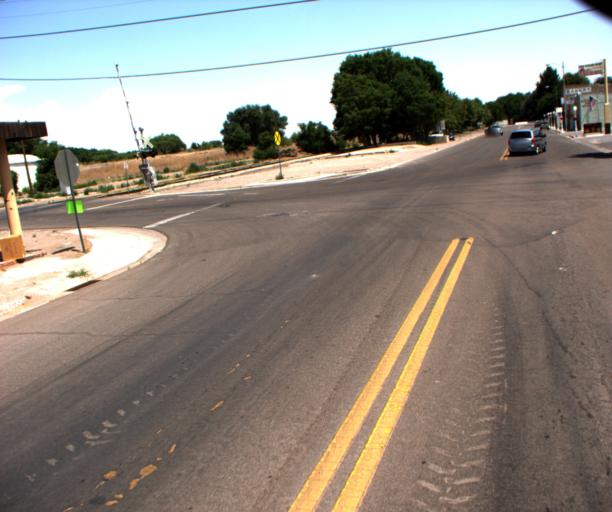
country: US
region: Arizona
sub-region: Greenlee County
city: Clifton
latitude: 32.7218
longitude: -109.1048
